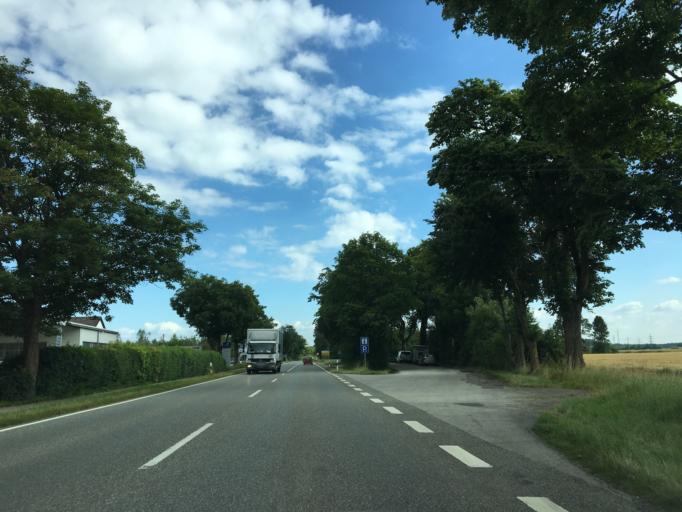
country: DE
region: Bavaria
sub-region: Upper Bavaria
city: Sauerlach
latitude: 47.9467
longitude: 11.6505
